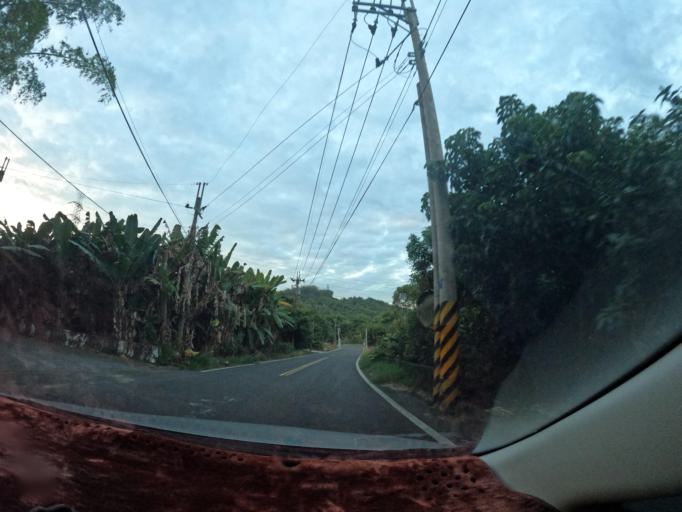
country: TW
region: Taiwan
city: Yujing
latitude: 23.0194
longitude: 120.4150
